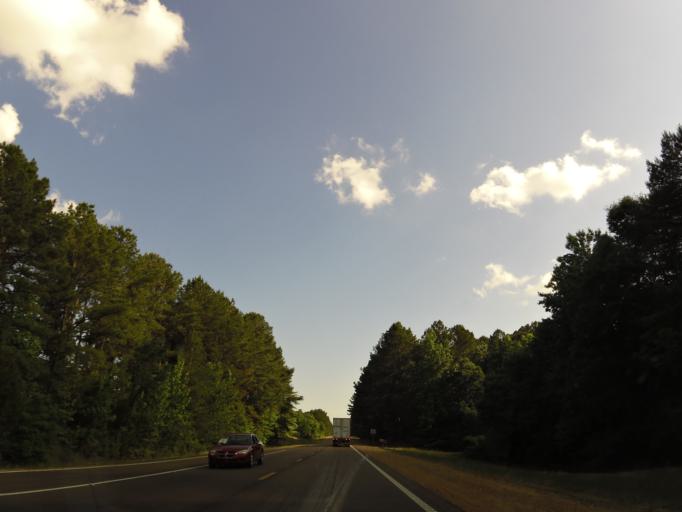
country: US
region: Mississippi
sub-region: Lafayette County
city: University
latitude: 34.2981
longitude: -89.5202
